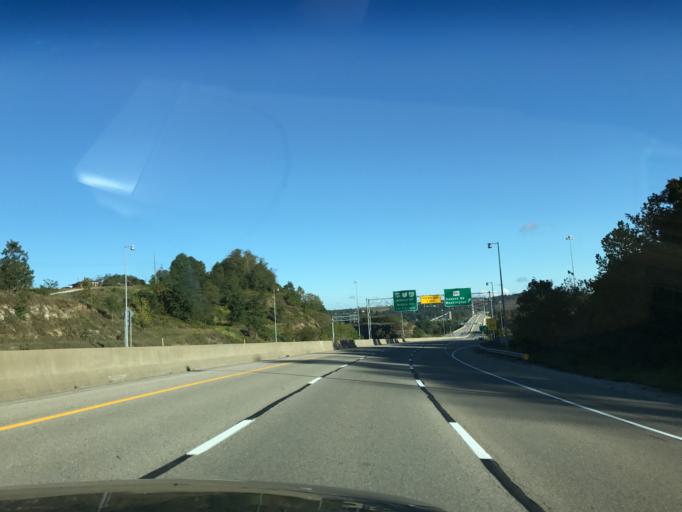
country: US
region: West Virginia
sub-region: Wood County
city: Blennerhassett
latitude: 39.2608
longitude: -81.6458
